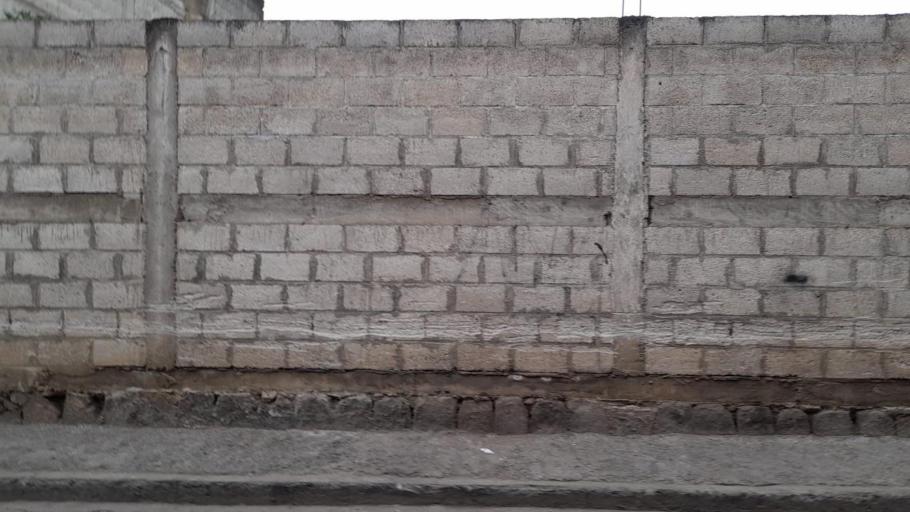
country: GT
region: Quetzaltenango
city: Quetzaltenango
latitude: 14.8309
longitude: -91.5119
